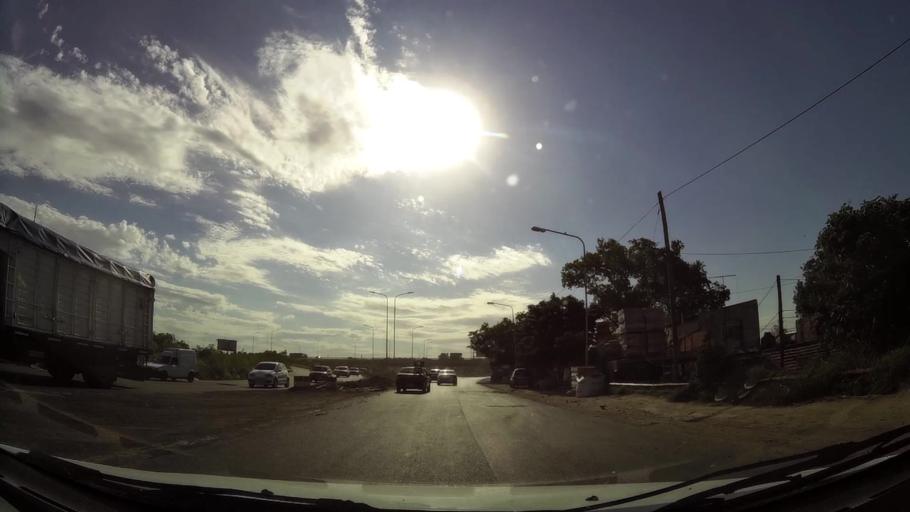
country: AR
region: Buenos Aires
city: Hurlingham
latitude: -34.5629
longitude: -58.6259
